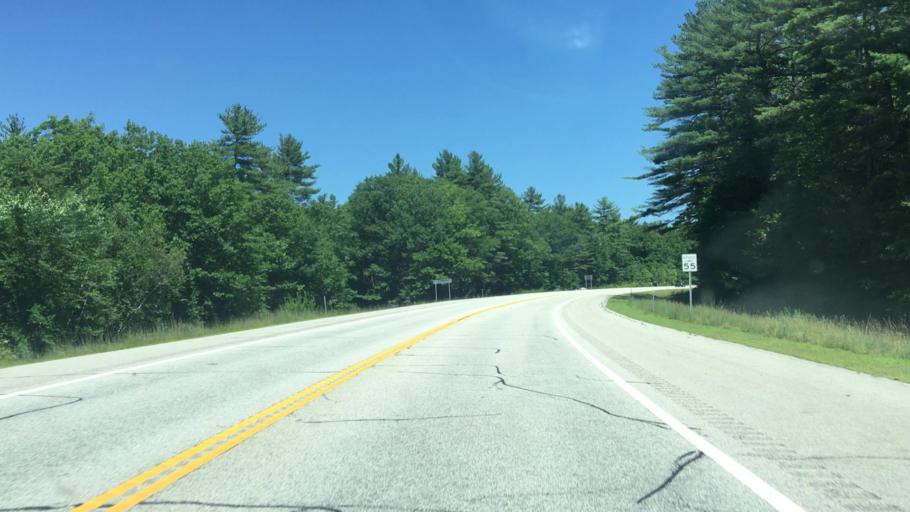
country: US
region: New Hampshire
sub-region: Merrimack County
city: Contoocook
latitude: 43.1803
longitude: -71.7390
